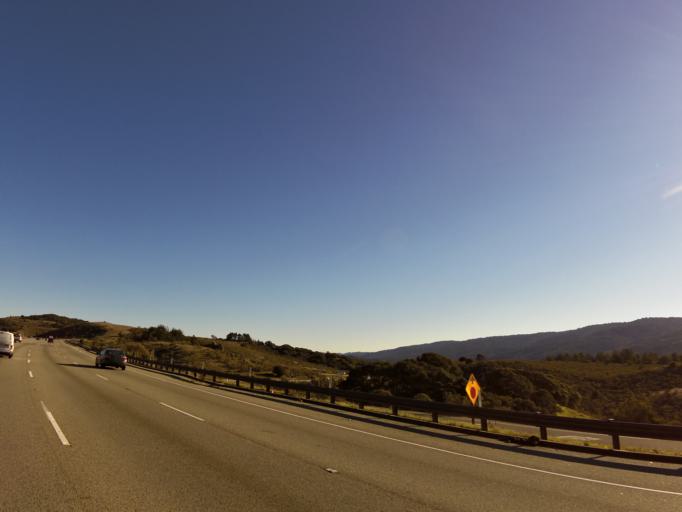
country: US
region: California
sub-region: San Mateo County
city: Highlands-Baywood Park
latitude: 37.4991
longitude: -122.3175
